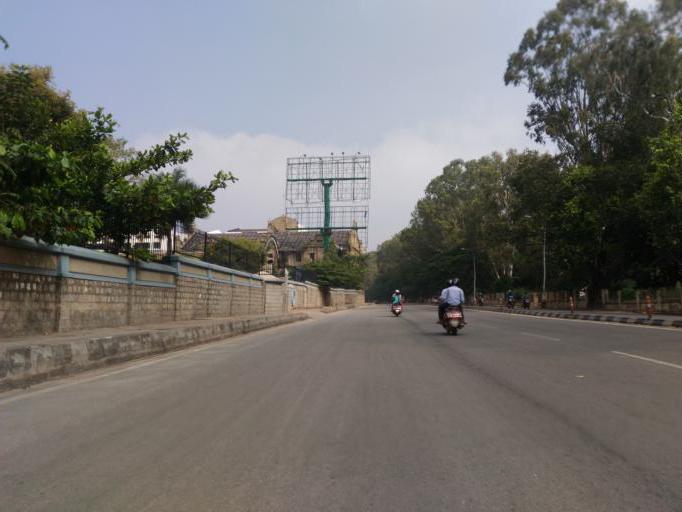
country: IN
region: Karnataka
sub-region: Bangalore Urban
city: Bangalore
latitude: 12.9604
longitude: 77.6064
